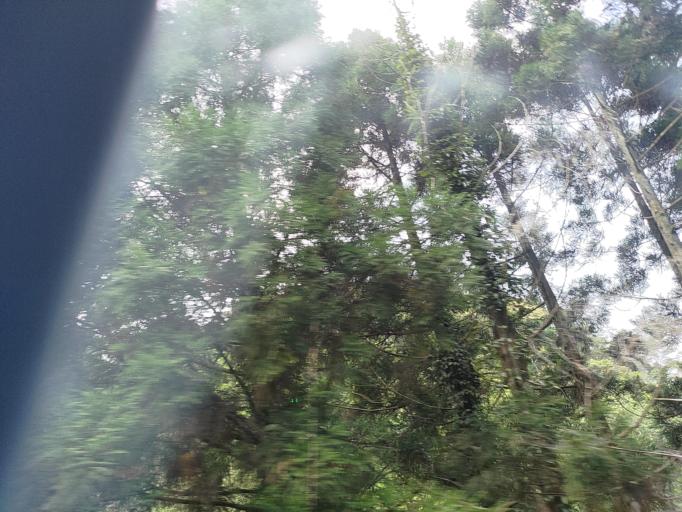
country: TW
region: Taiwan
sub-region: Hsinchu
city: Hsinchu
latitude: 24.6198
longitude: 121.0500
